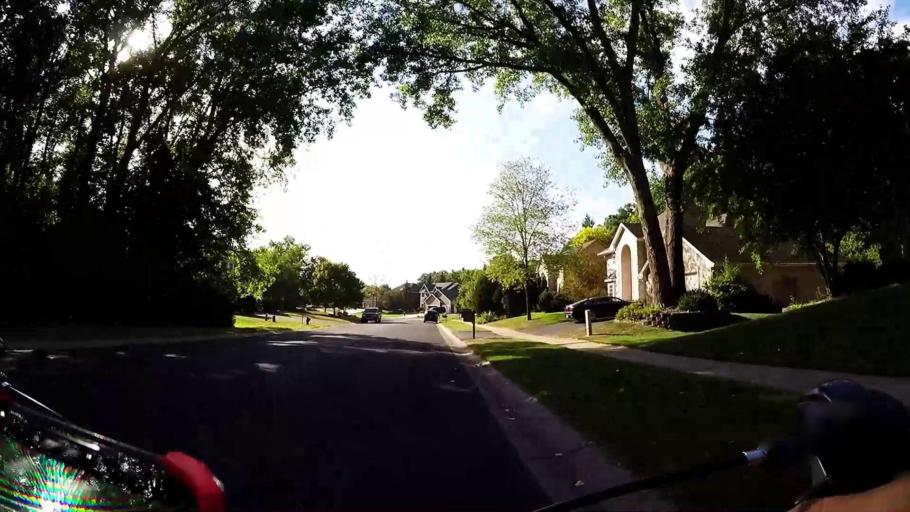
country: US
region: Minnesota
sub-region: Hennepin County
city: Eden Prairie
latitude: 44.8837
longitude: -93.4457
